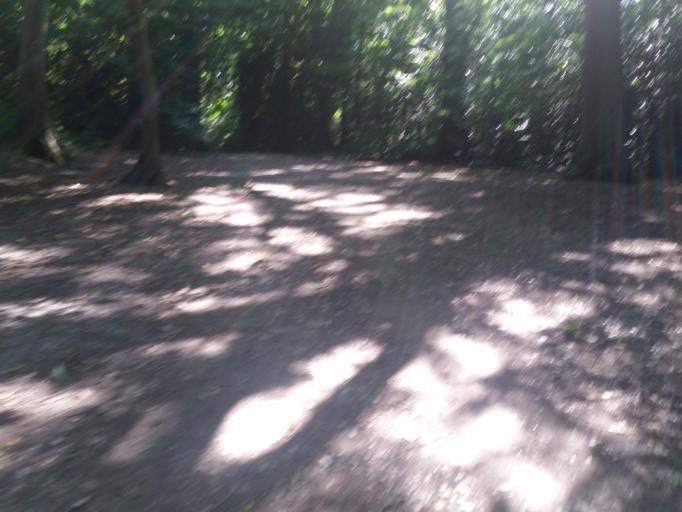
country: GB
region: England
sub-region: Greater London
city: Crouch End
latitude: 51.5844
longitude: -0.1523
